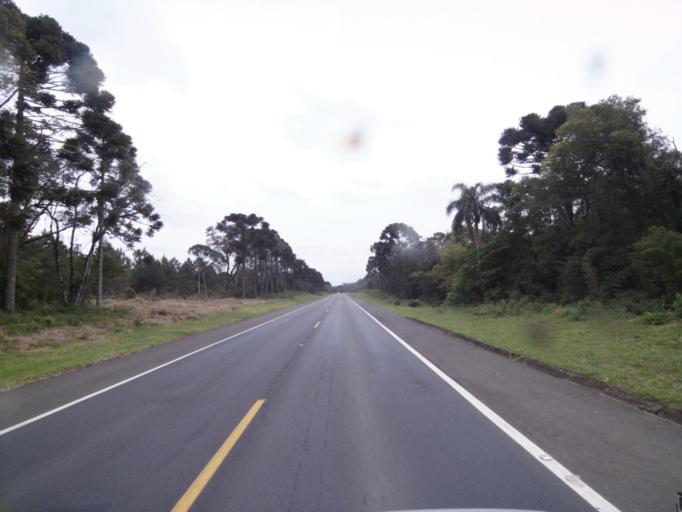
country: BR
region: Parana
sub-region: Irati
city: Irati
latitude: -25.4687
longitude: -50.5054
